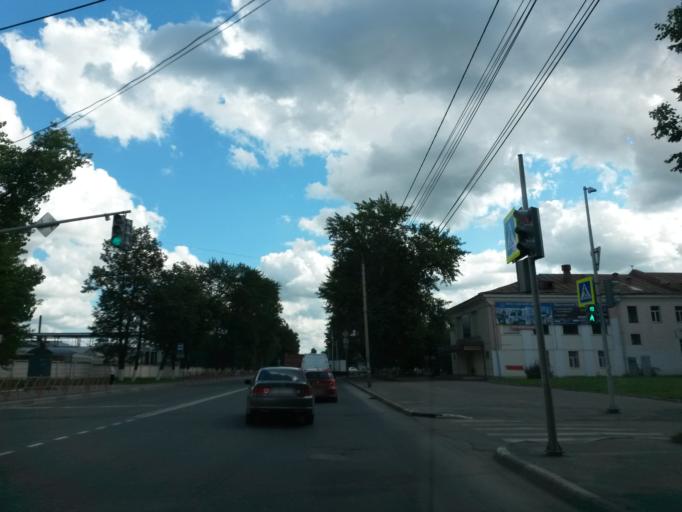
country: RU
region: Jaroslavl
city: Yaroslavl
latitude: 57.6096
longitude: 39.8719
